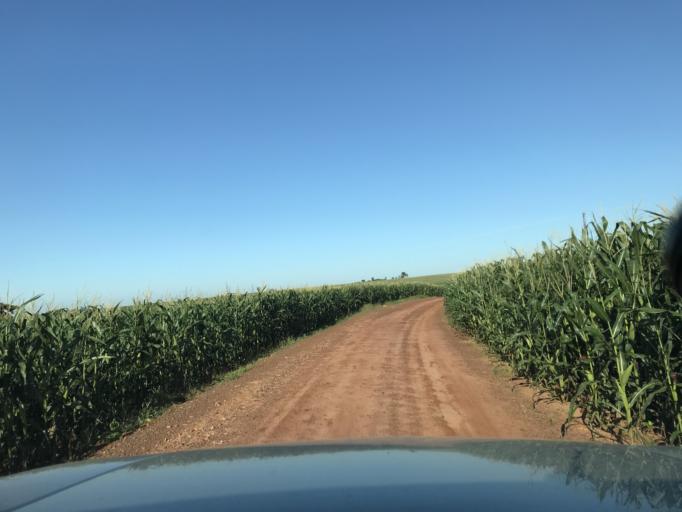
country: BR
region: Parana
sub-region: Palotina
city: Palotina
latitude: -24.2329
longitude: -53.7695
